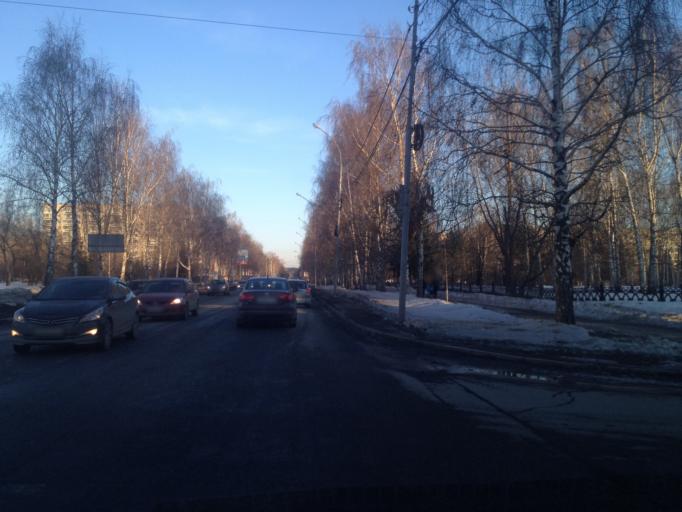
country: RU
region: Sverdlovsk
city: Sovkhoznyy
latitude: 56.8039
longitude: 60.5630
